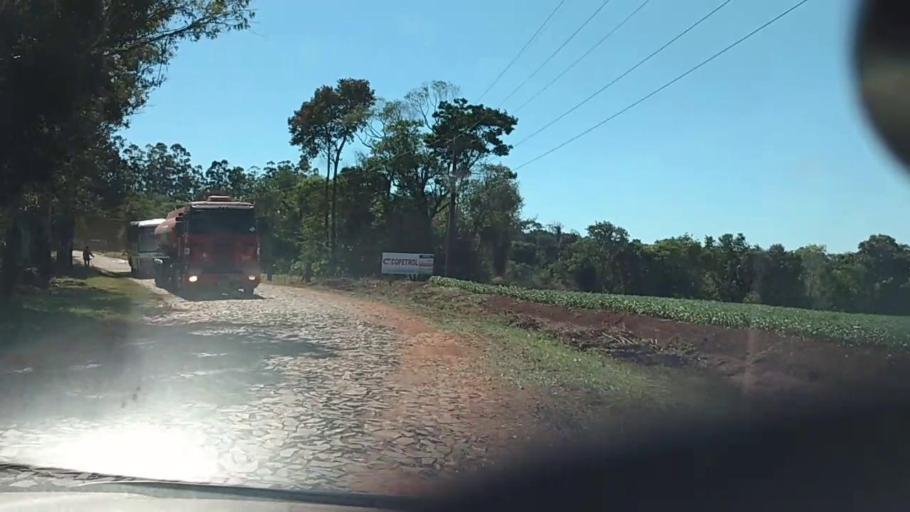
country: PY
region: Alto Parana
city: Naranjal
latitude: -25.9622
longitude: -55.1430
